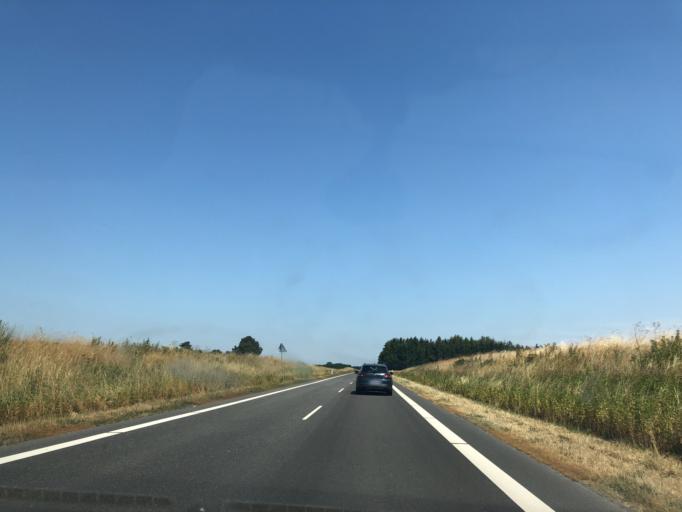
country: DK
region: Zealand
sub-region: Slagelse Kommune
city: Skaelskor
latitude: 55.2393
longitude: 11.3160
